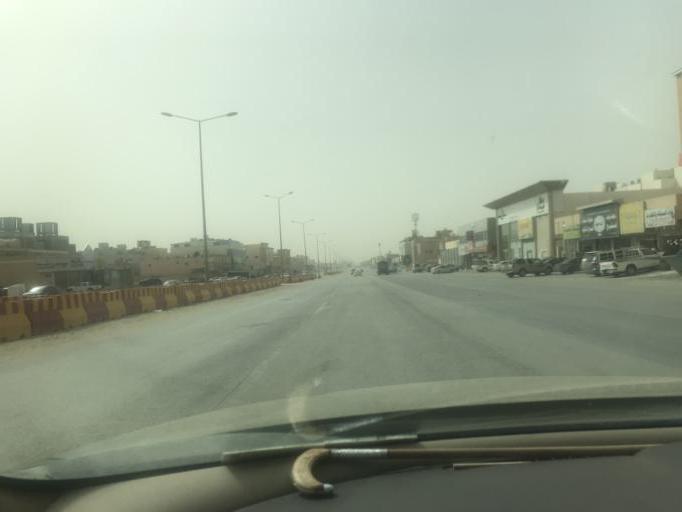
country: SA
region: Ar Riyad
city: Riyadh
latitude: 24.8100
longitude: 46.6006
